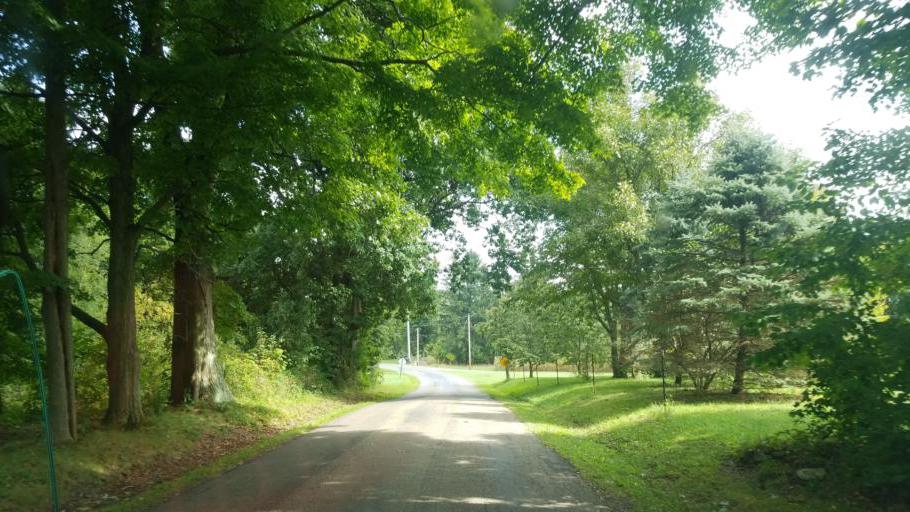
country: US
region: Ohio
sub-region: Knox County
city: Mount Vernon
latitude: 40.4668
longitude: -82.4624
